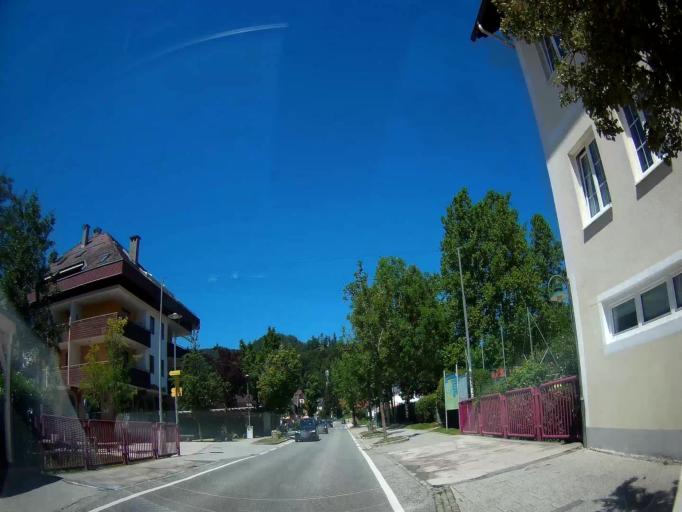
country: AT
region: Carinthia
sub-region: Politischer Bezirk Klagenfurt Land
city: Keutschach am See
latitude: 46.6068
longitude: 14.1808
